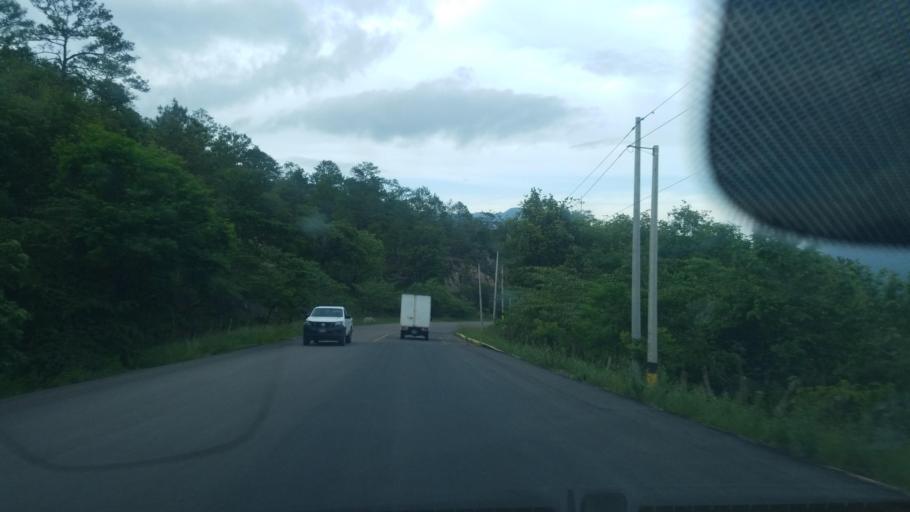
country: HN
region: Santa Barbara
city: Concepcion del Sur
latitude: 14.7964
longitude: -88.1566
